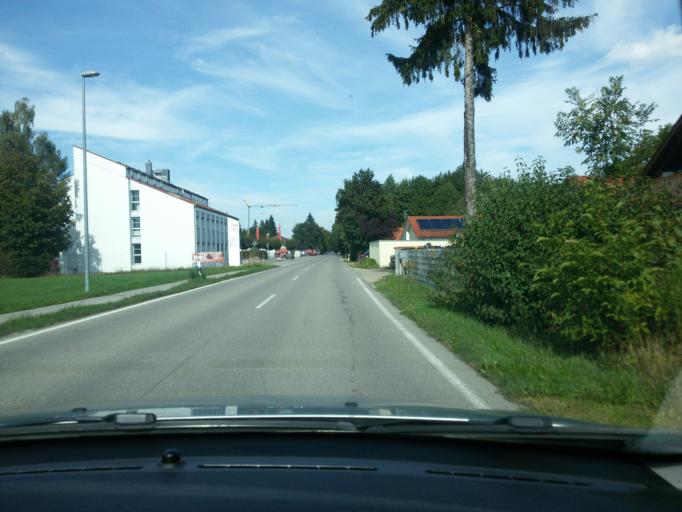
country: DE
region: Bavaria
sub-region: Swabia
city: Wehringen
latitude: 48.2618
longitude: 10.7875
